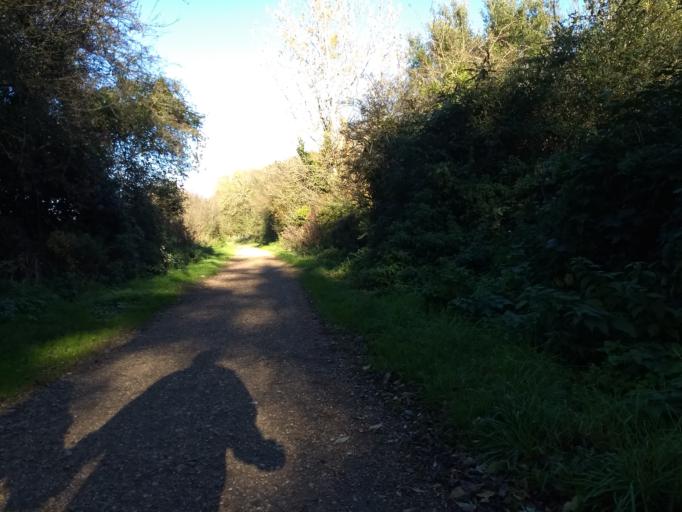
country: GB
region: England
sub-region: Isle of Wight
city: Newport
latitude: 50.6877
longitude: -1.2896
